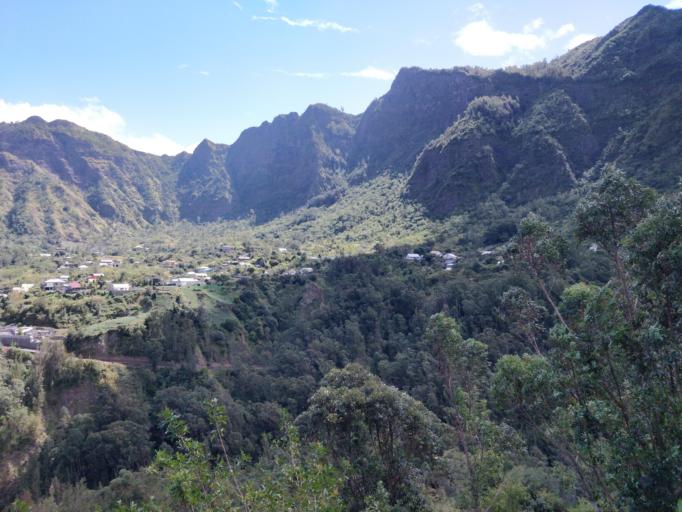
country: RE
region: Reunion
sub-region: Reunion
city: Cilaos
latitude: -21.1704
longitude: 55.4836
